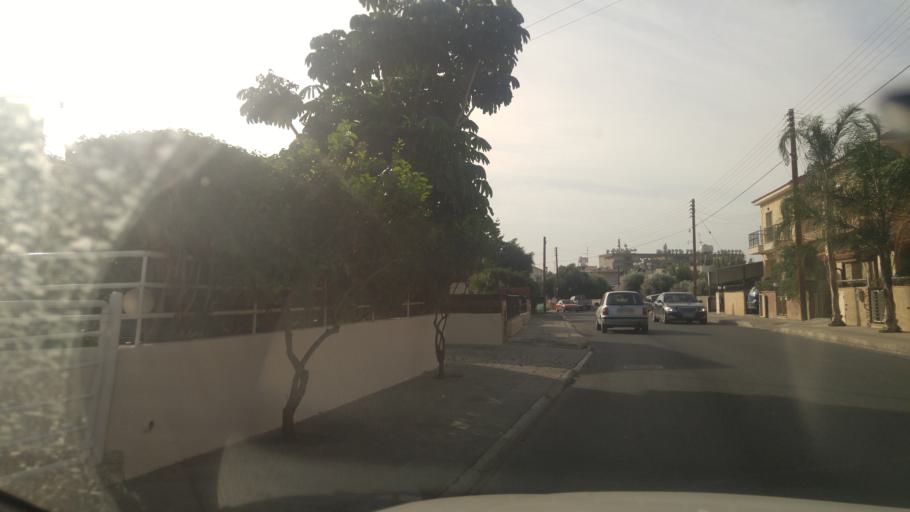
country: CY
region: Limassol
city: Limassol
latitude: 34.6609
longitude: 33.0028
